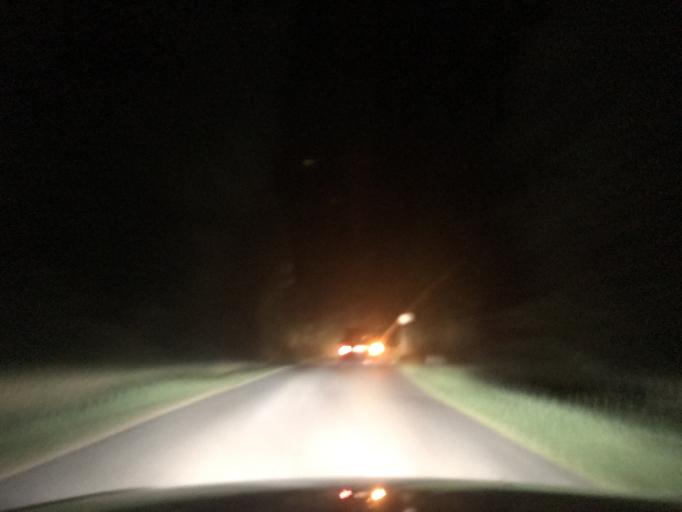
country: DE
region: Bavaria
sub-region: Upper Palatinate
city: Auerbach
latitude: 49.7088
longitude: 11.5952
